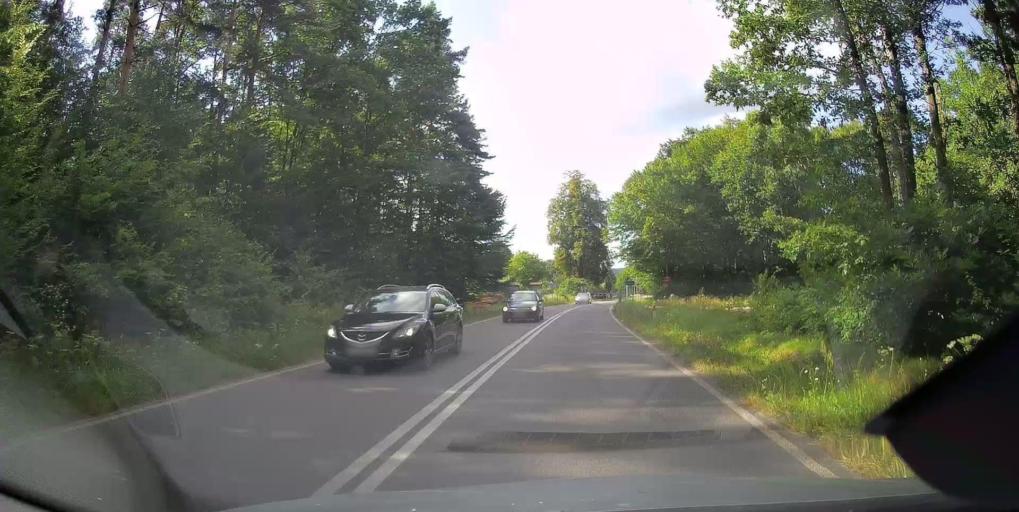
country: PL
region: Swietokrzyskie
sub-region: Powiat skarzyski
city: Laczna
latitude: 50.9970
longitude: 20.8521
